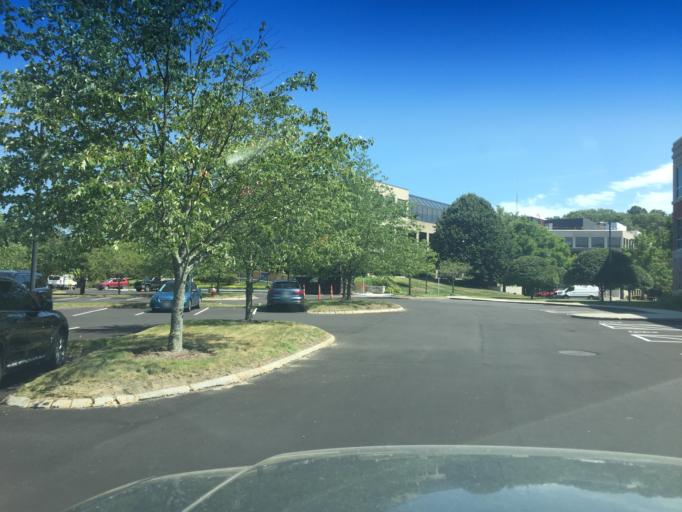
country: US
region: Massachusetts
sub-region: Norfolk County
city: Needham
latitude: 42.3158
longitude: -71.2375
